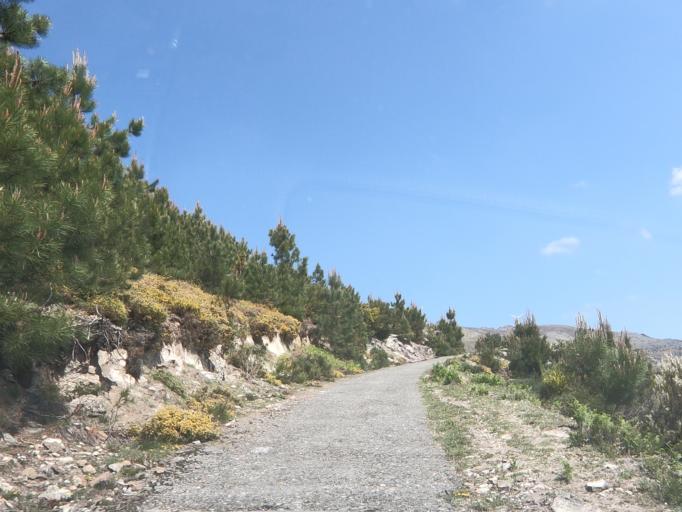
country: PT
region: Vila Real
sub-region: Vila Real
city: Vila Real
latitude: 41.3644
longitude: -7.7401
